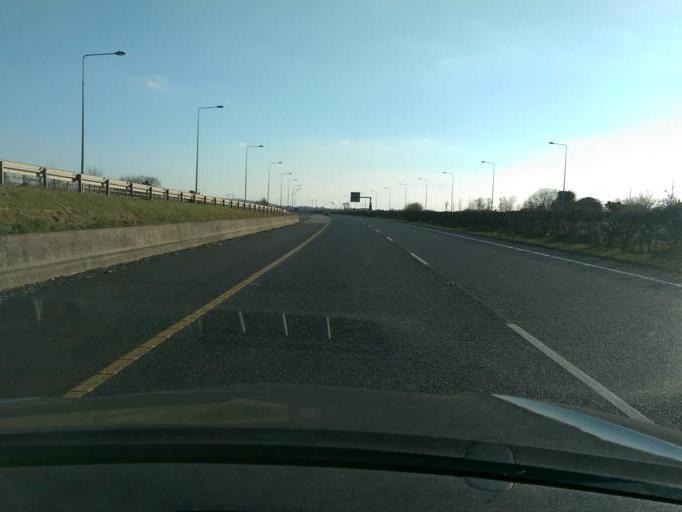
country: IE
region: Leinster
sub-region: Laois
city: Portlaoise
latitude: 53.0478
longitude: -7.2410
